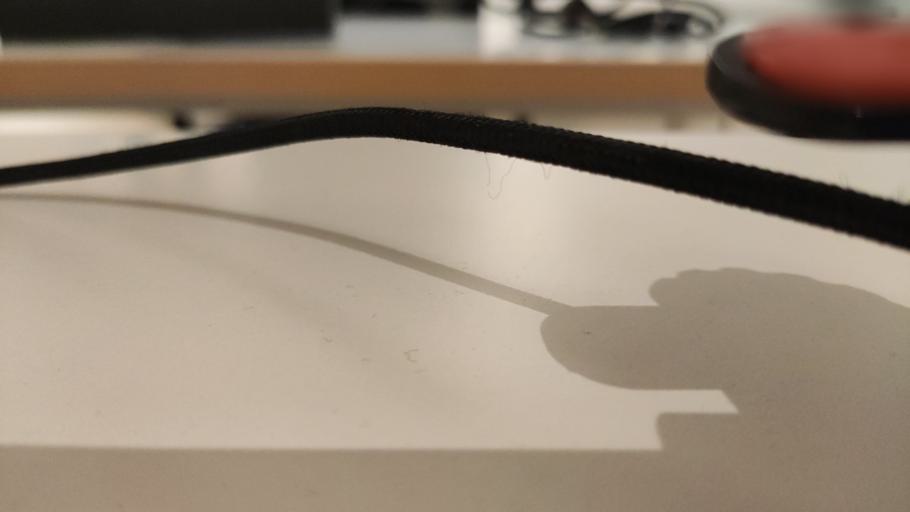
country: RU
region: Moskovskaya
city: Dorokhovo
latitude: 55.5124
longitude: 36.3479
